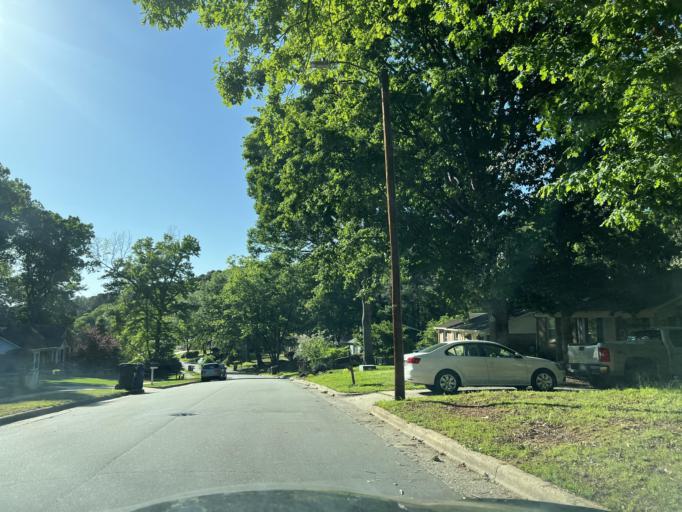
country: US
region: North Carolina
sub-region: Wake County
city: West Raleigh
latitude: 35.8640
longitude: -78.6392
